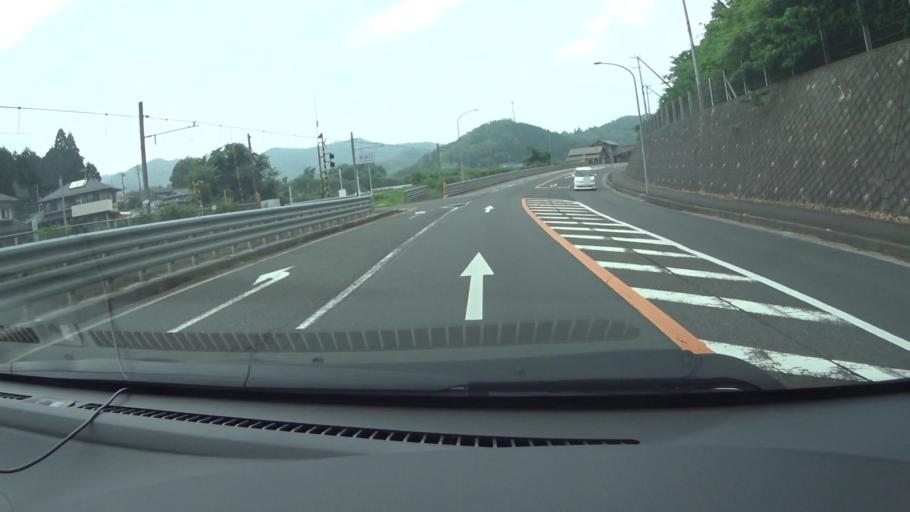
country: JP
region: Kyoto
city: Ayabe
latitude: 35.3516
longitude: 135.3107
